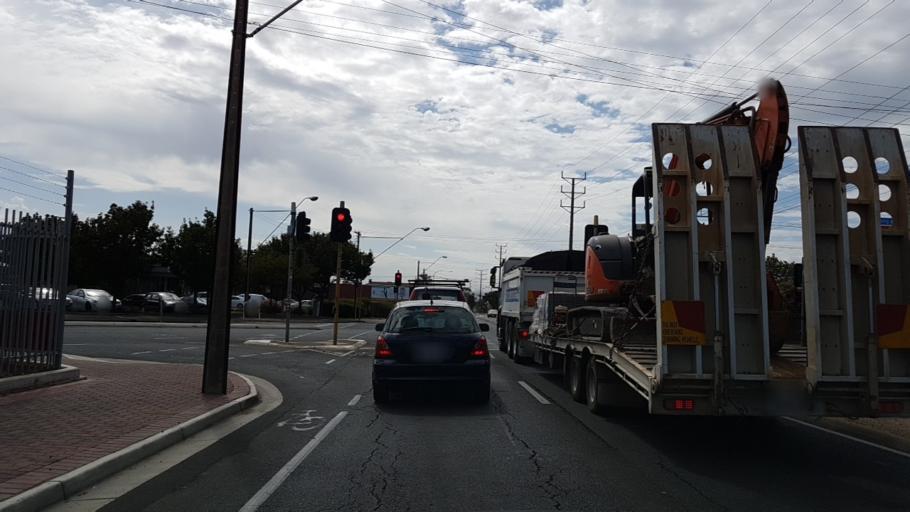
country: AU
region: South Australia
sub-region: Charles Sturt
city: Allenby Gardens
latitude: -34.9047
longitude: 138.5458
